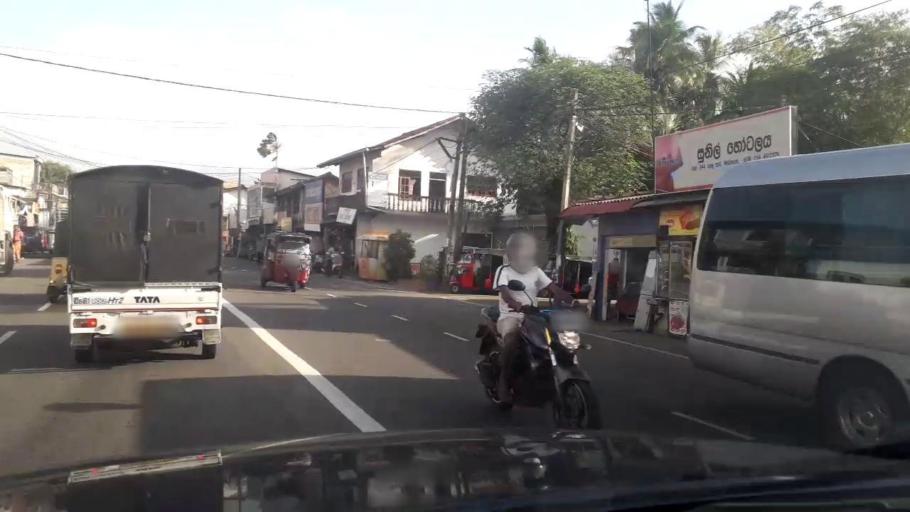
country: LK
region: Western
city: Beruwala
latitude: 6.5055
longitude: 79.9809
